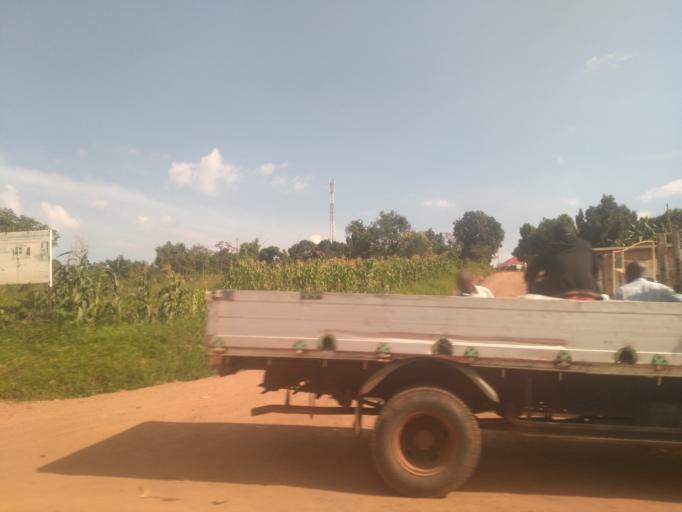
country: UG
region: Central Region
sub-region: Wakiso District
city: Kajansi
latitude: 0.2782
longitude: 32.4694
